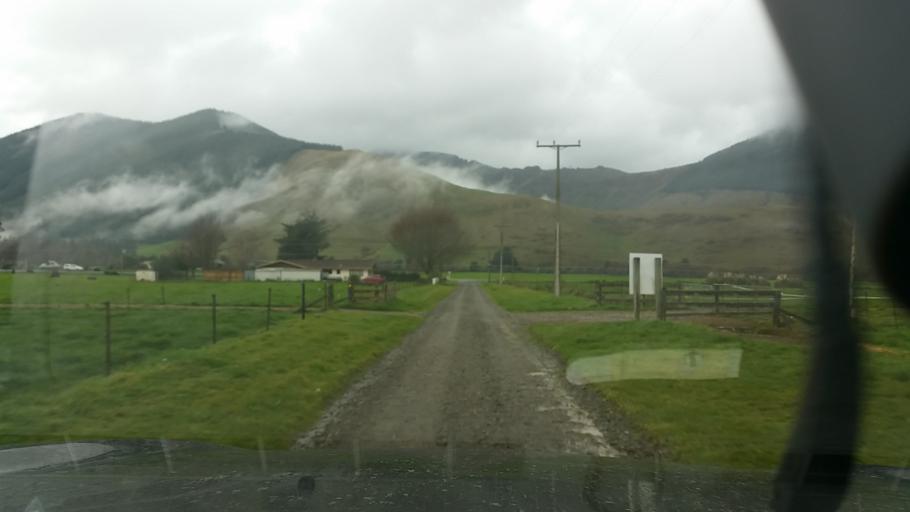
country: NZ
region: Nelson
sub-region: Nelson City
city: Nelson
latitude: -41.2383
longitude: 173.5772
